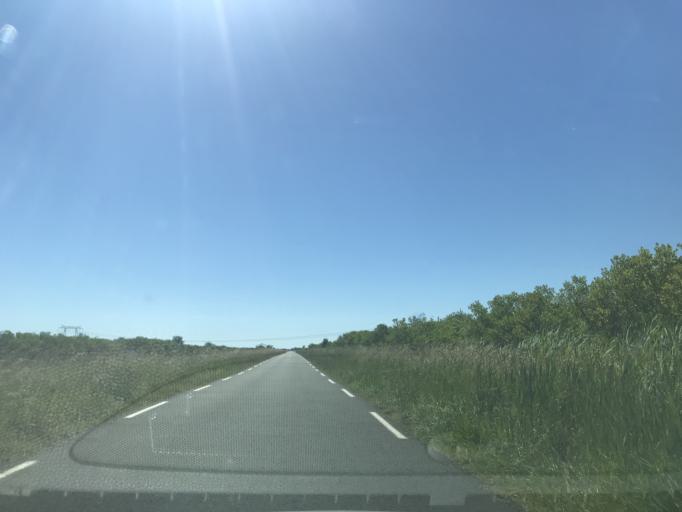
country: FR
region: Aquitaine
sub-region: Departement de la Gironde
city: Saint-Ciers-sur-Gironde
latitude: 45.2894
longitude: -0.6519
